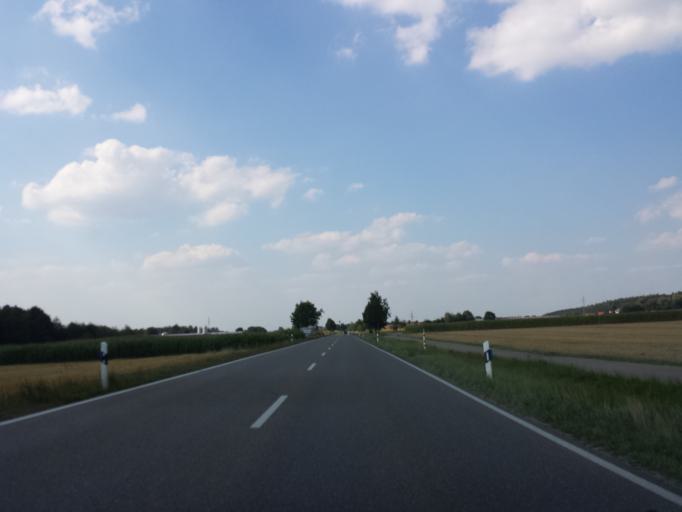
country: DE
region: Bavaria
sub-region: Swabia
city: Ichenhausen
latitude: 48.3988
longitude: 10.3032
